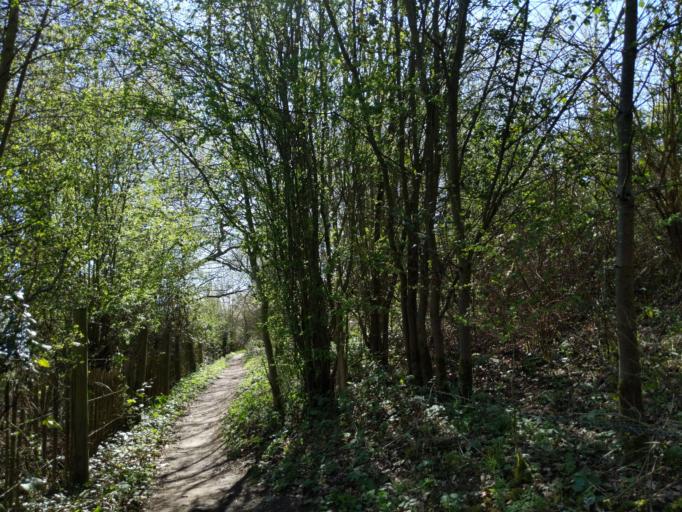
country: GB
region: England
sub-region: Surrey
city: Esher
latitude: 51.3776
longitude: -0.3787
